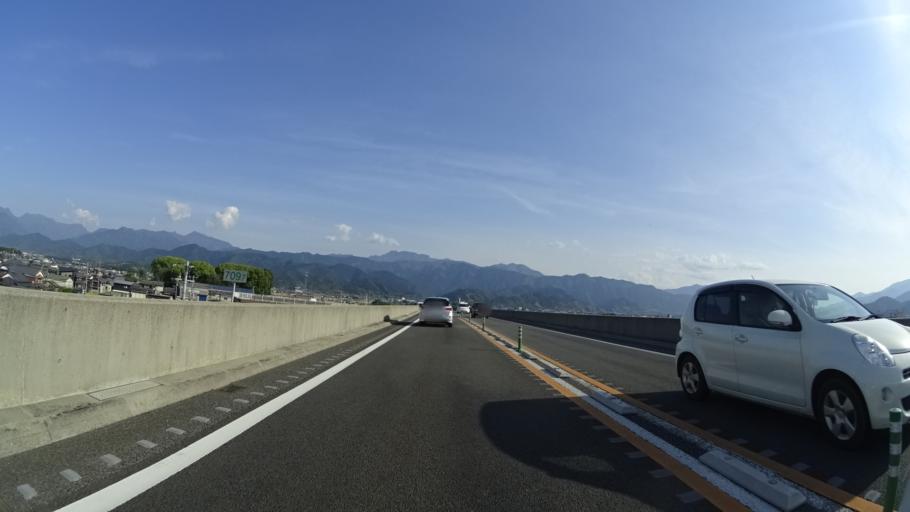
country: JP
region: Ehime
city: Saijo
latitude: 33.9126
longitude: 133.0730
